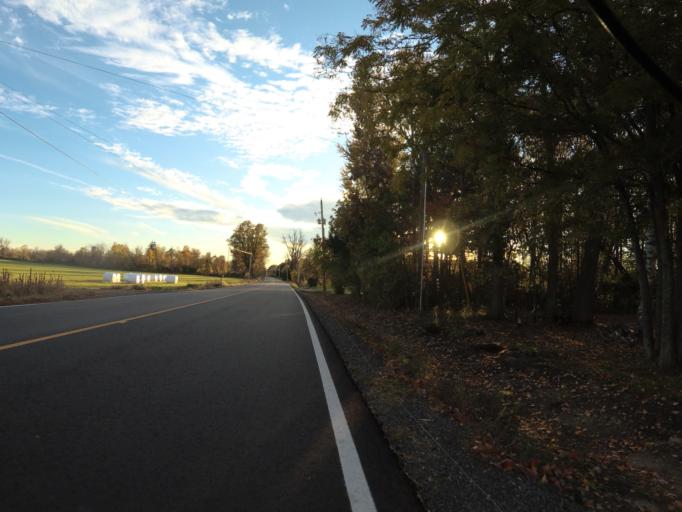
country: CA
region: Ontario
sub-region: Lanark County
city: Smiths Falls
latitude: 44.9603
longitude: -75.8125
